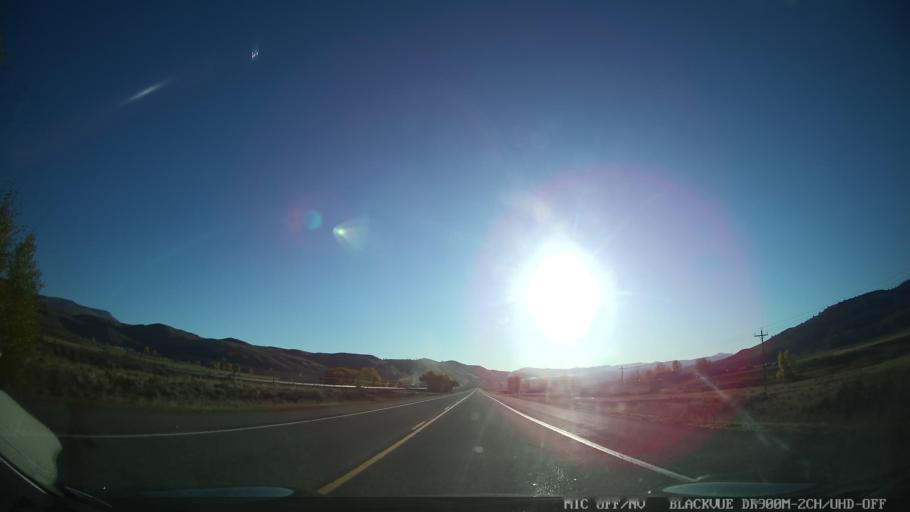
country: US
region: Colorado
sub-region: Grand County
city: Hot Sulphur Springs
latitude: 40.0673
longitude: -106.2167
